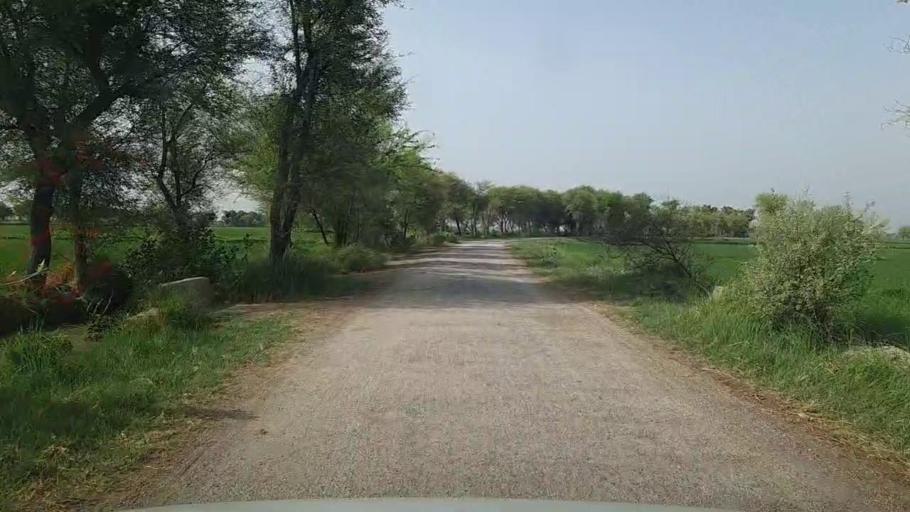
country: PK
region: Sindh
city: Mehar
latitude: 27.1203
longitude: 67.8223
